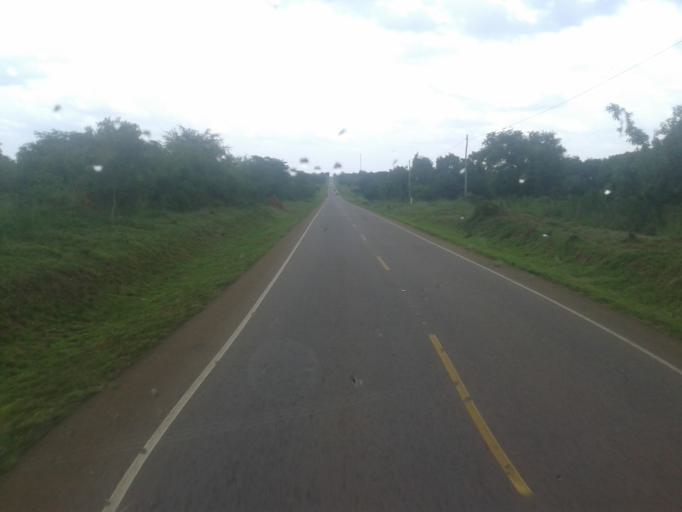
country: UG
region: Central Region
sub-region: Nakasongola District
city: Nakasongola
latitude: 1.3463
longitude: 32.3891
